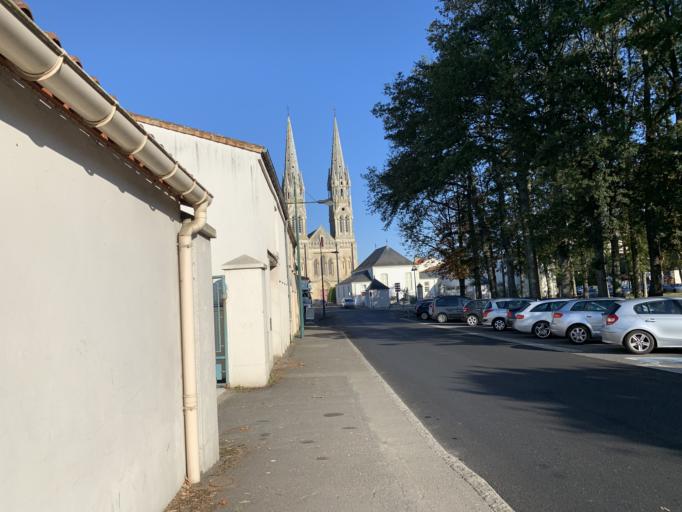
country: FR
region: Pays de la Loire
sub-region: Departement de la Loire-Atlantique
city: Machecoul
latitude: 46.9914
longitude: -1.8166
